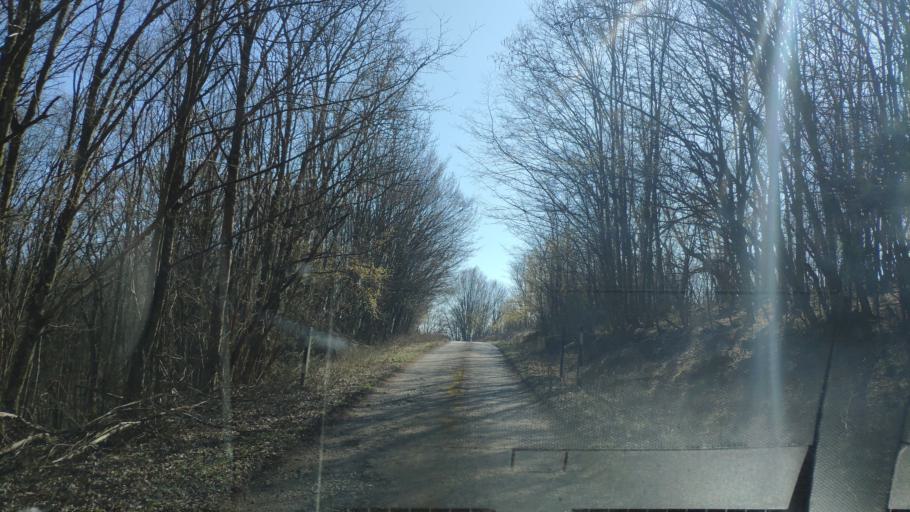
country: SK
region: Kosicky
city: Roznava
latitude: 48.5842
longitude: 20.4049
